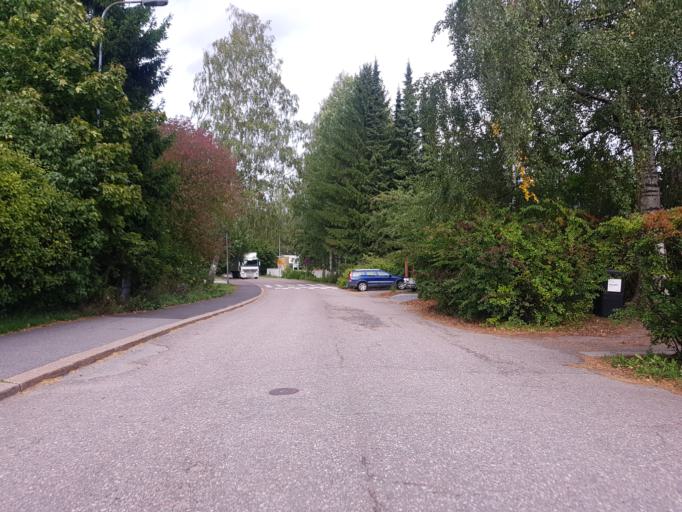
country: FI
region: Uusimaa
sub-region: Helsinki
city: Helsinki
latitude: 60.2295
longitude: 24.9573
